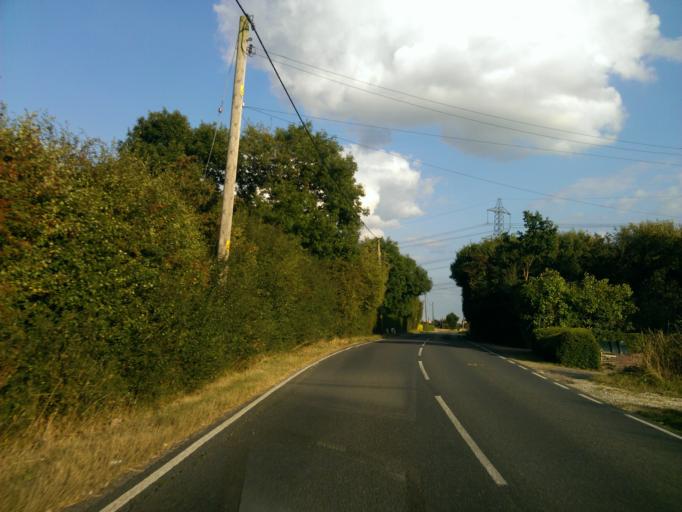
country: GB
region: England
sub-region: Essex
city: Rayne
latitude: 51.8645
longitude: 0.5900
